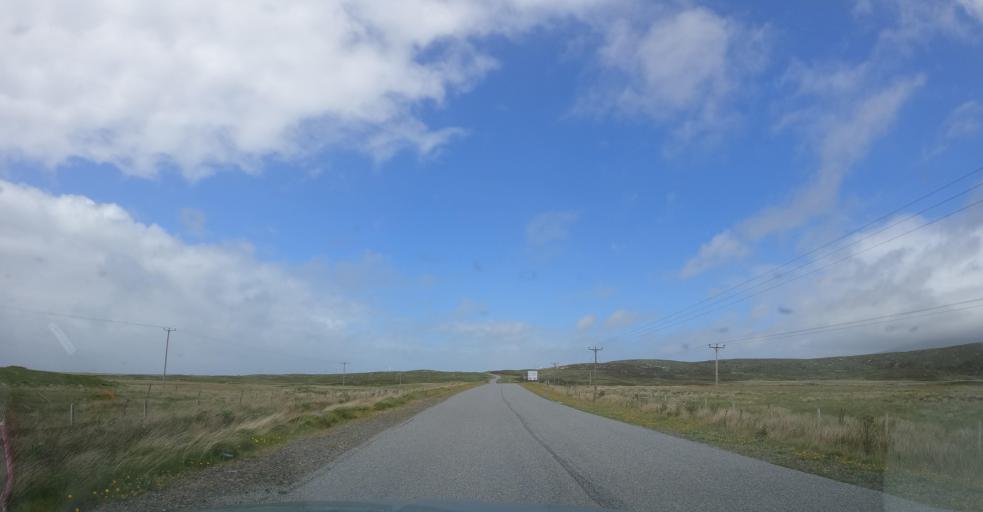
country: GB
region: Scotland
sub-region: Eilean Siar
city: Isle of South Uist
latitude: 57.2254
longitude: -7.3943
